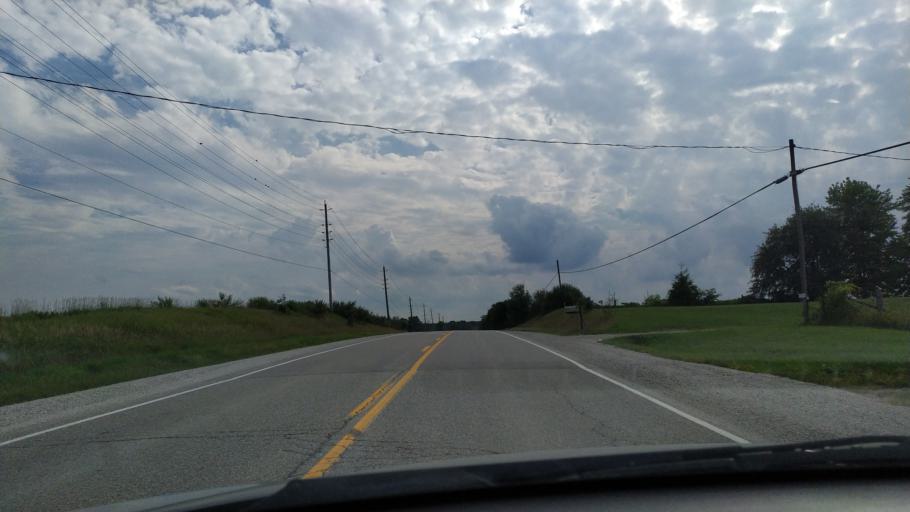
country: CA
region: Ontario
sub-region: Wellington County
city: Guelph
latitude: 43.4648
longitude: -80.1660
